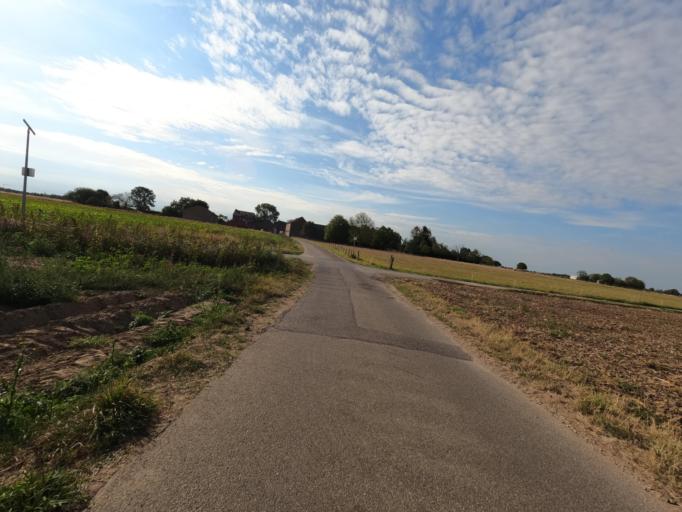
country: DE
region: North Rhine-Westphalia
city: Wegberg
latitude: 51.1081
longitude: 6.2505
